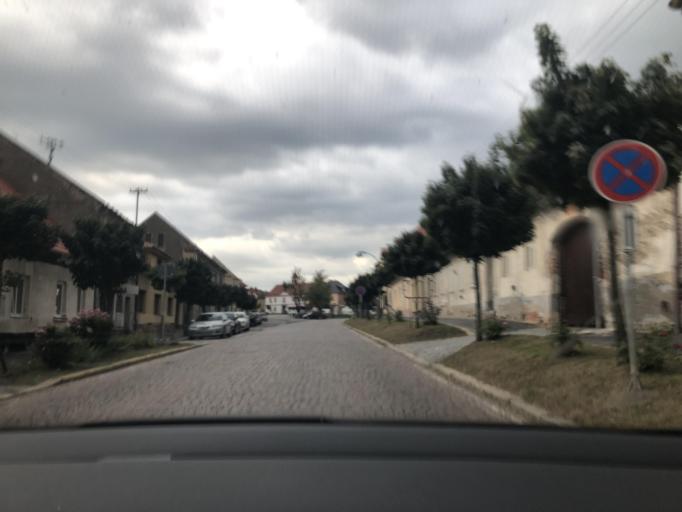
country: CZ
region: Central Bohemia
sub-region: Okres Kolin
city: Tynec nad Labem
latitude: 50.0434
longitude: 15.3585
